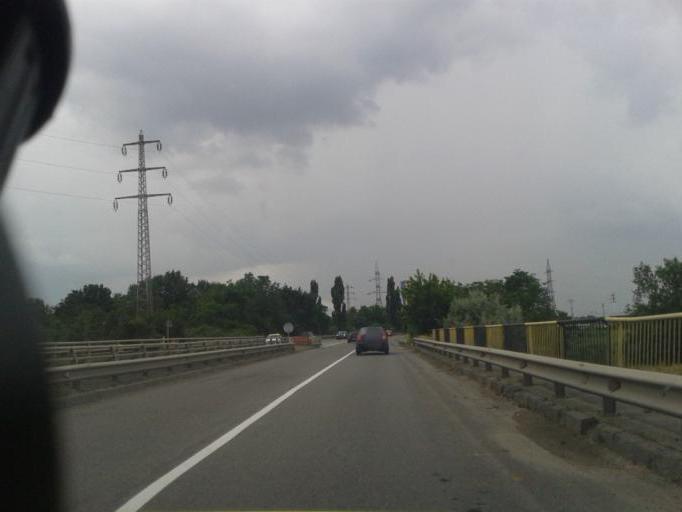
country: RO
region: Prahova
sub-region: Comuna Bucov
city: Bucov
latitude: 44.9642
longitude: 26.0611
